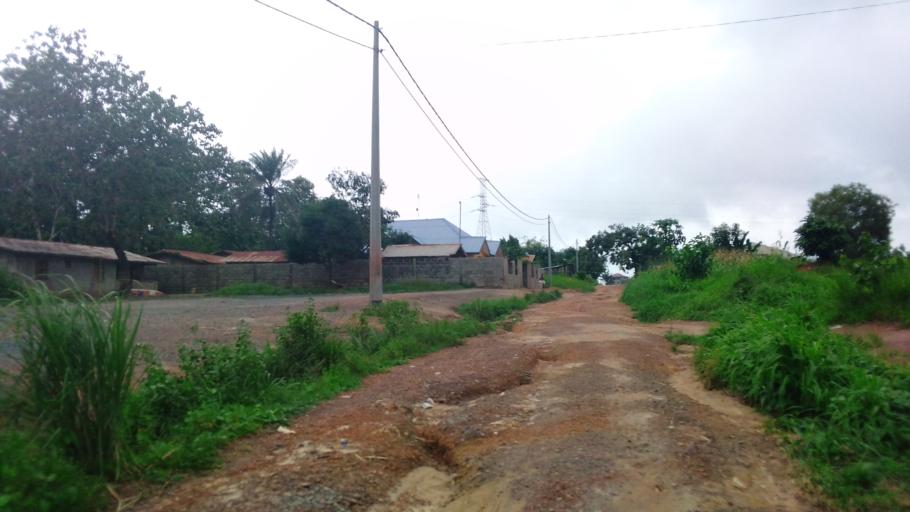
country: SL
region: Northern Province
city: Lunsar
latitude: 8.6908
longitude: -12.5472
